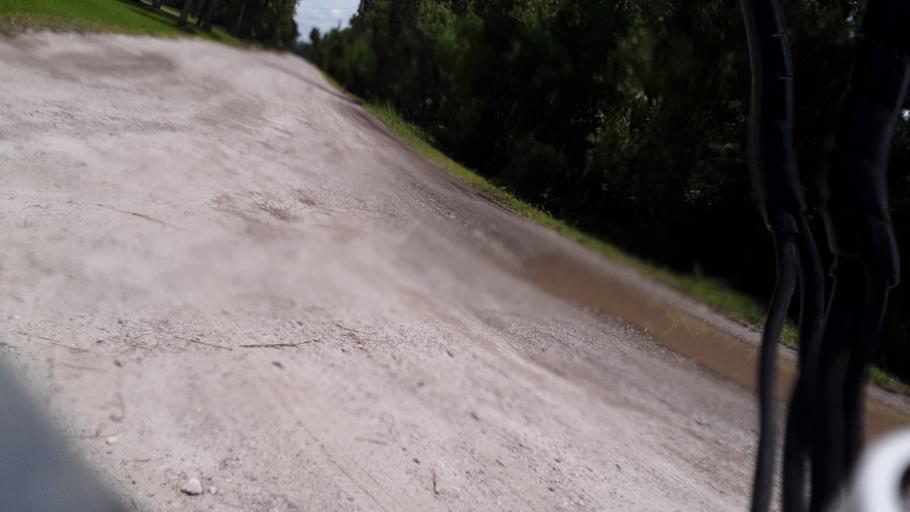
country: US
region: Florida
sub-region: Brevard County
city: Malabar
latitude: 27.9909
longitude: -80.6018
